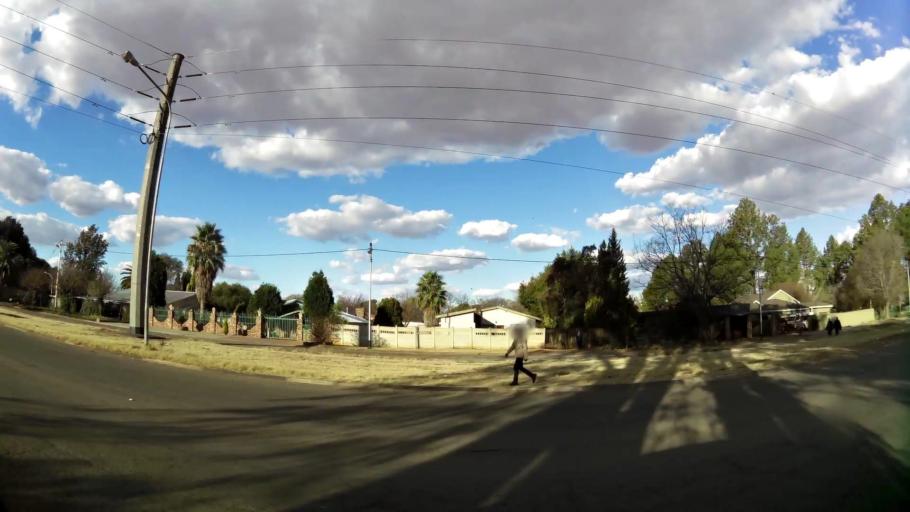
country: ZA
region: North-West
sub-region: Dr Kenneth Kaunda District Municipality
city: Potchefstroom
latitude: -26.7002
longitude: 27.0786
